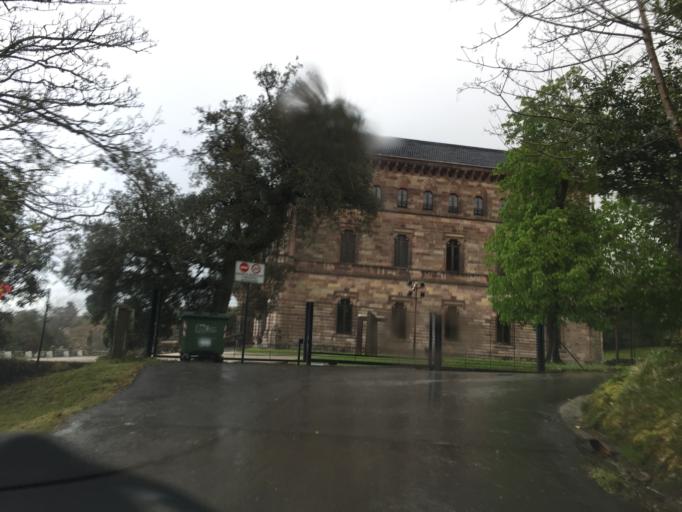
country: ES
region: Cantabria
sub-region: Provincia de Cantabria
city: Comillas
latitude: 43.3837
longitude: -4.2953
